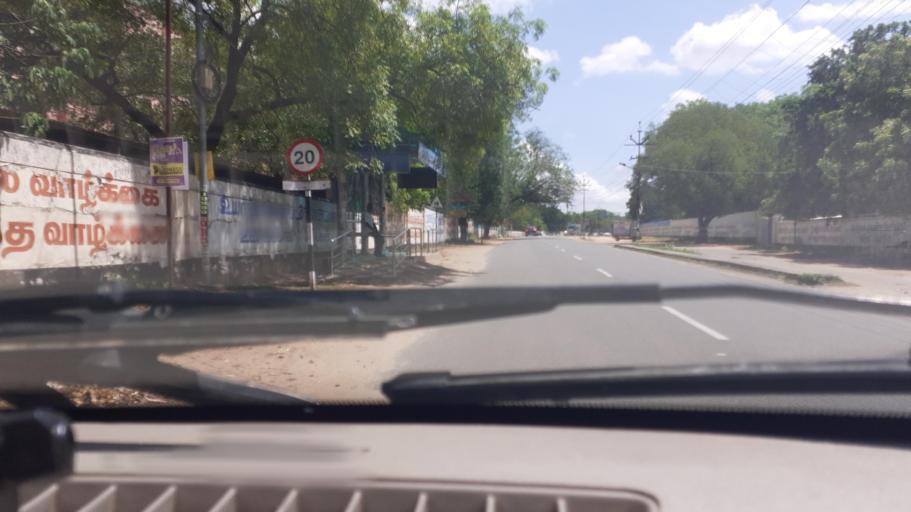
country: IN
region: Tamil Nadu
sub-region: Tirunelveli Kattabo
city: Tirunelveli
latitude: 8.7187
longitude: 77.7372
